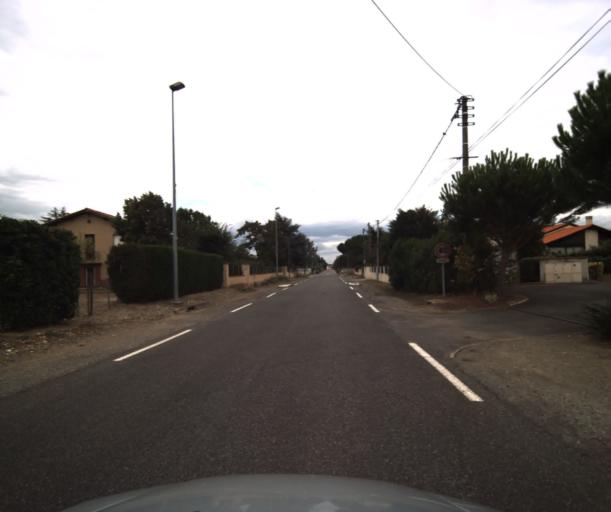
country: FR
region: Midi-Pyrenees
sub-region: Departement de la Haute-Garonne
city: Muret
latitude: 43.4513
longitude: 1.3177
